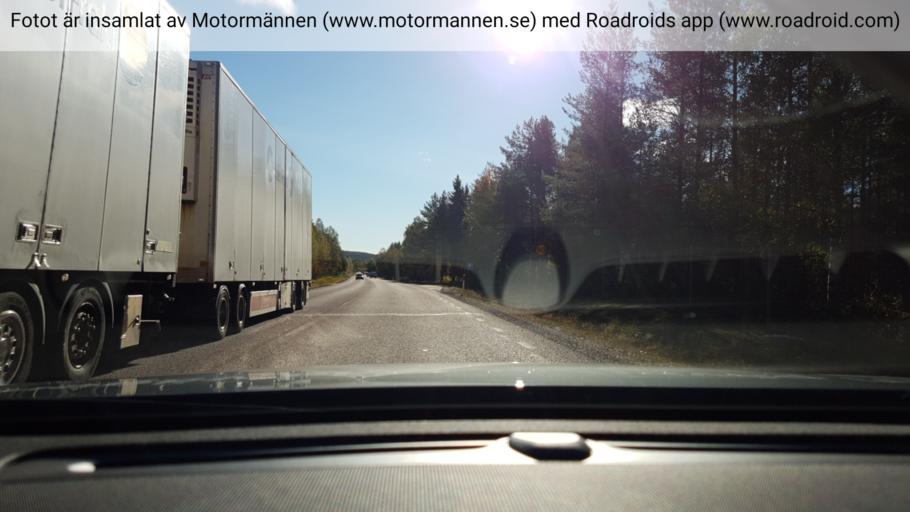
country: SE
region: Vaesterbotten
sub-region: Skelleftea Kommun
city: Burea
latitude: 64.6122
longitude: 21.1840
